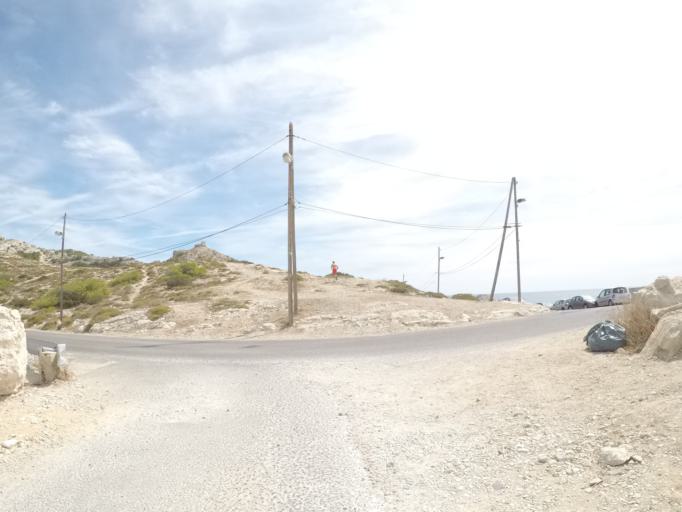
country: FR
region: Provence-Alpes-Cote d'Azur
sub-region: Departement des Bouches-du-Rhone
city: Marseille 08
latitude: 43.2134
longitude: 5.3494
